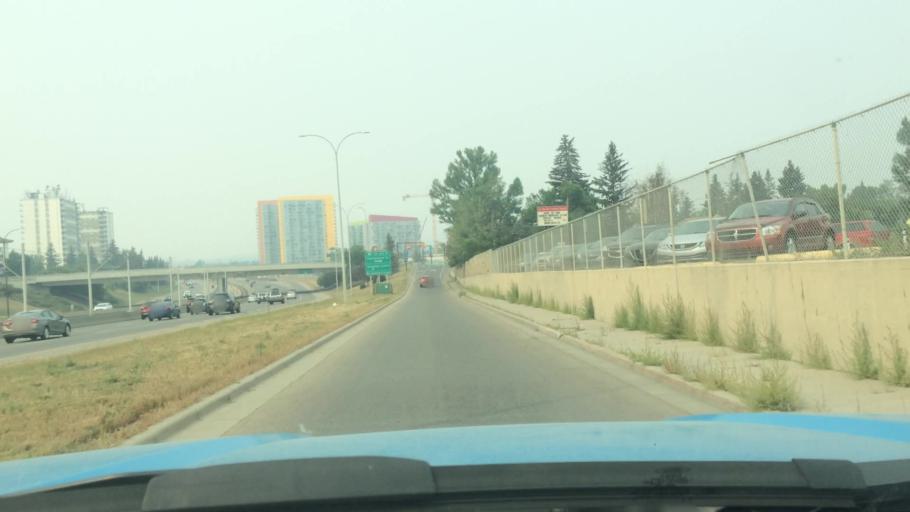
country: CA
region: Alberta
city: Calgary
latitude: 51.0813
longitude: -114.1235
